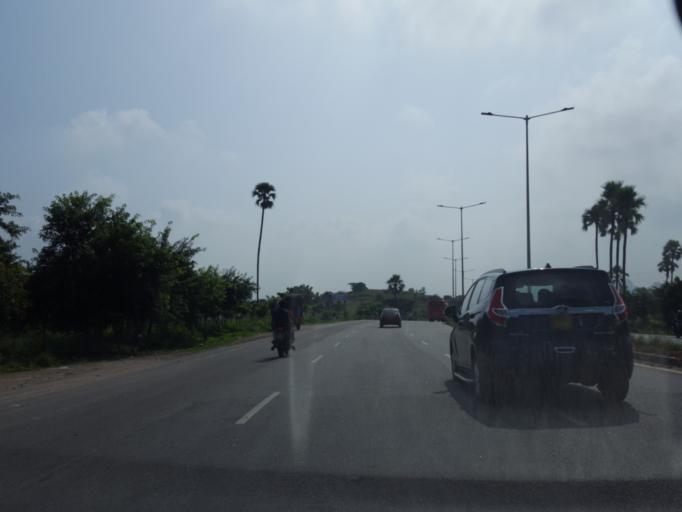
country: IN
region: Telangana
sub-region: Rangareddi
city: Ghatkesar
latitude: 17.3089
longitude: 78.6997
